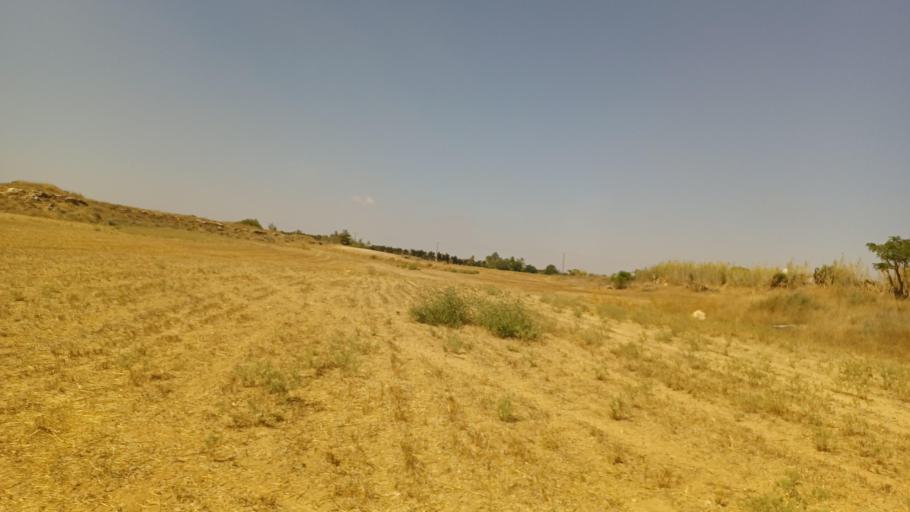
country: CY
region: Ammochostos
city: Acheritou
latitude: 35.0697
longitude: 33.8641
